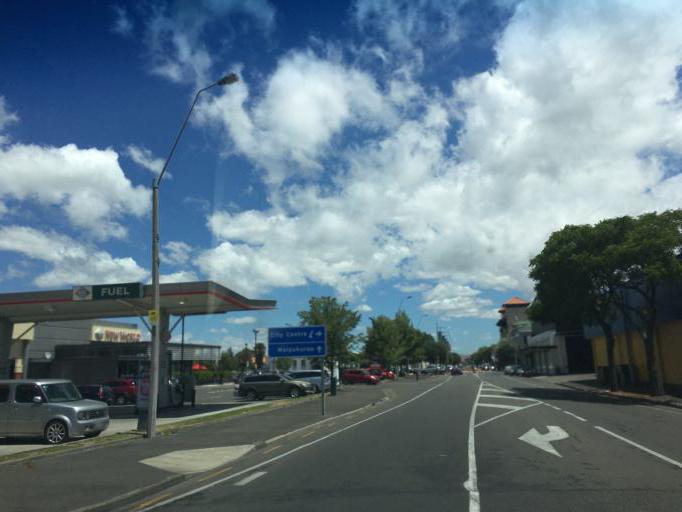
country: NZ
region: Hawke's Bay
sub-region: Hastings District
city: Hastings
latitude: -39.6441
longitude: 176.8473
